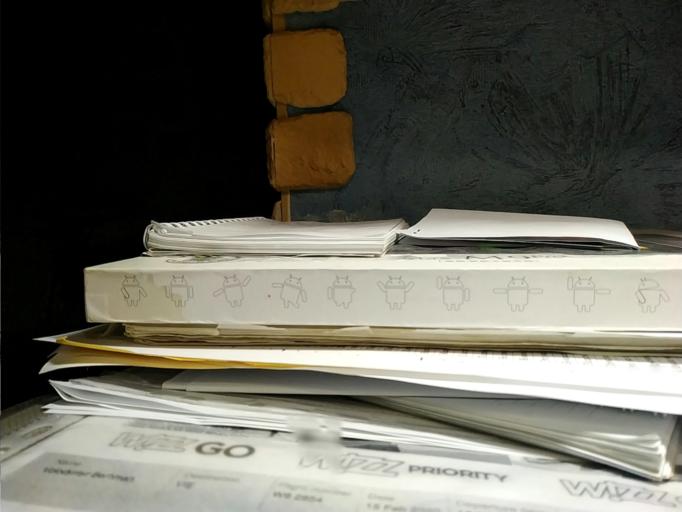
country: RU
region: Arkhangelskaya
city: Konevo
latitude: 62.7321
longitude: 38.5978
